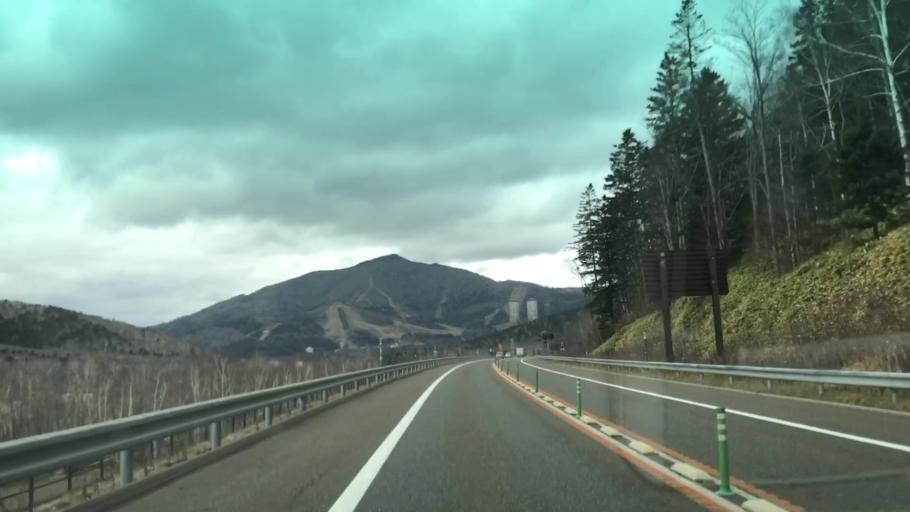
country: JP
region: Hokkaido
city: Shimo-furano
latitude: 43.0469
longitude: 142.6536
